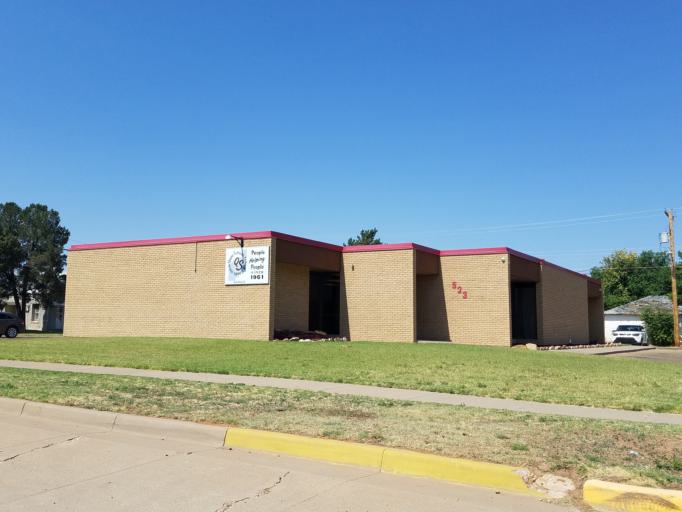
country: US
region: New Mexico
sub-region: Quay County
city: Tucumcari
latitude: 35.1750
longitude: -103.7262
